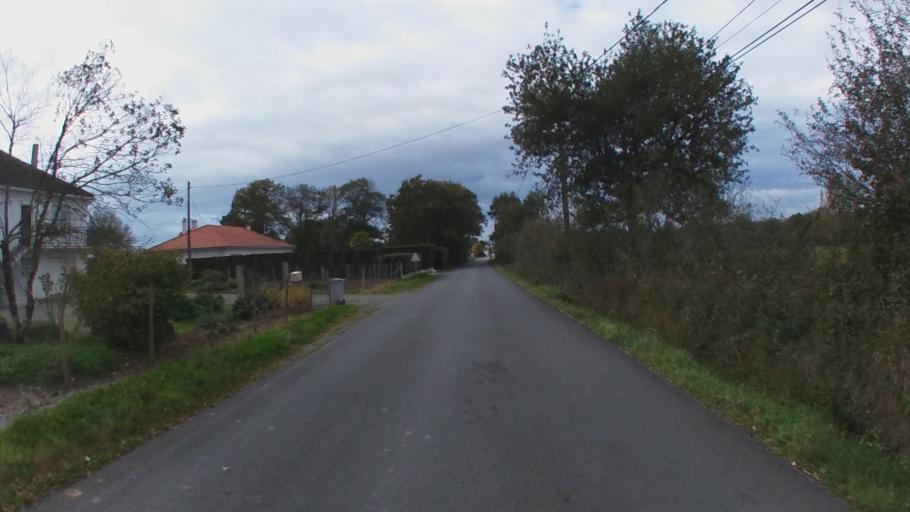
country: FR
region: Pays de la Loire
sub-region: Departement de la Loire-Atlantique
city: Saint-Brevin-les-Pins
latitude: 47.2525
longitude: -2.1338
